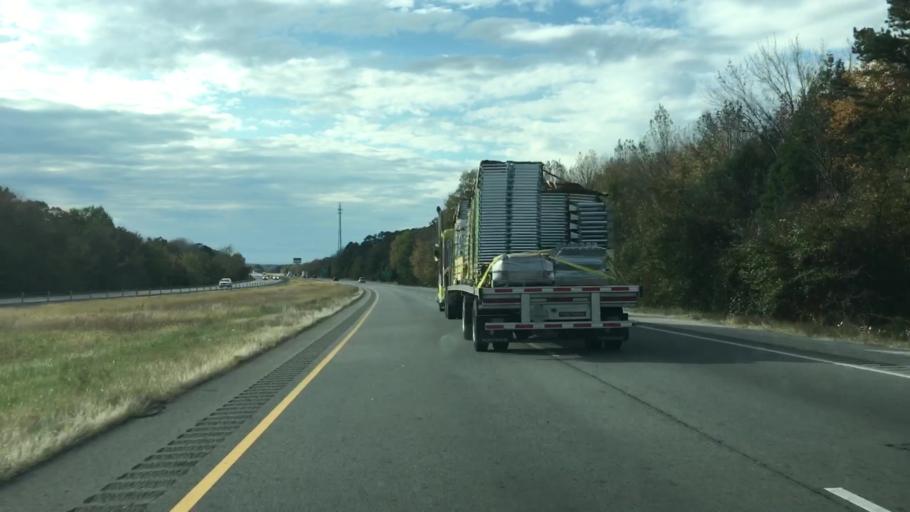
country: US
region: Arkansas
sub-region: Pope County
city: Pottsville
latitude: 35.2476
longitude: -93.0075
